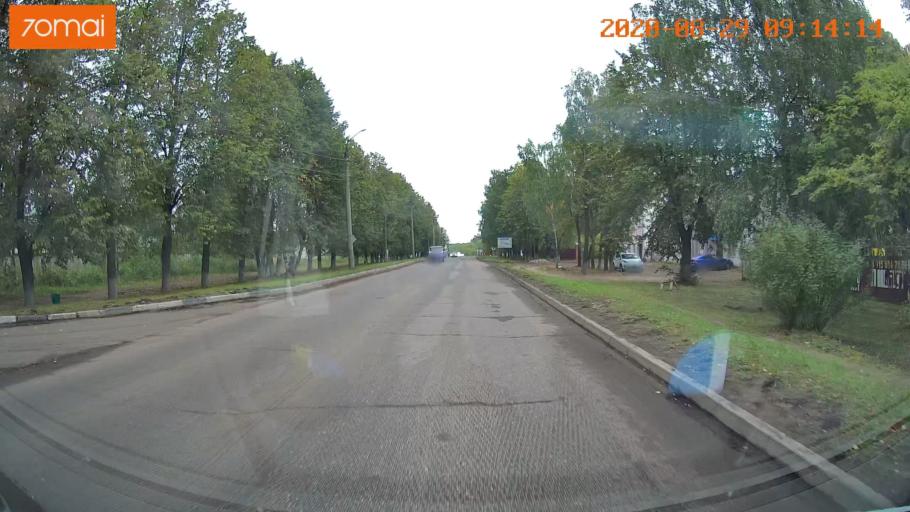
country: RU
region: Ivanovo
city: Kineshma
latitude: 57.4347
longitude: 42.1150
